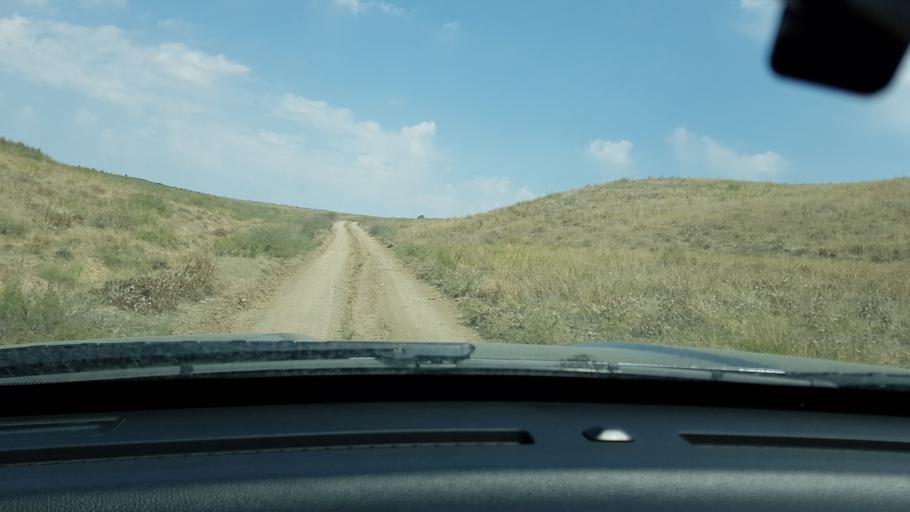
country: TM
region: Ahal
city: Baharly
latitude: 38.4083
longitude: 56.9121
